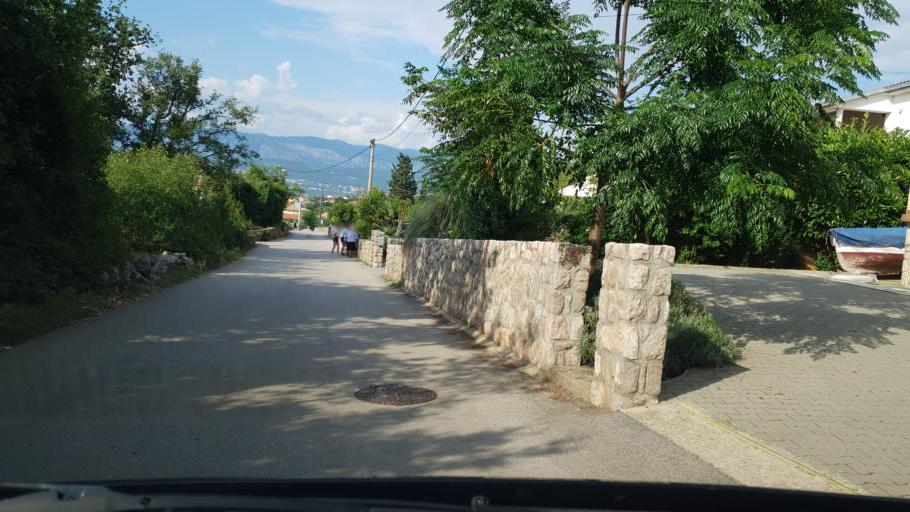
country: HR
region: Primorsko-Goranska
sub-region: Grad Crikvenica
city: Jadranovo
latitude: 45.1524
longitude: 14.6174
